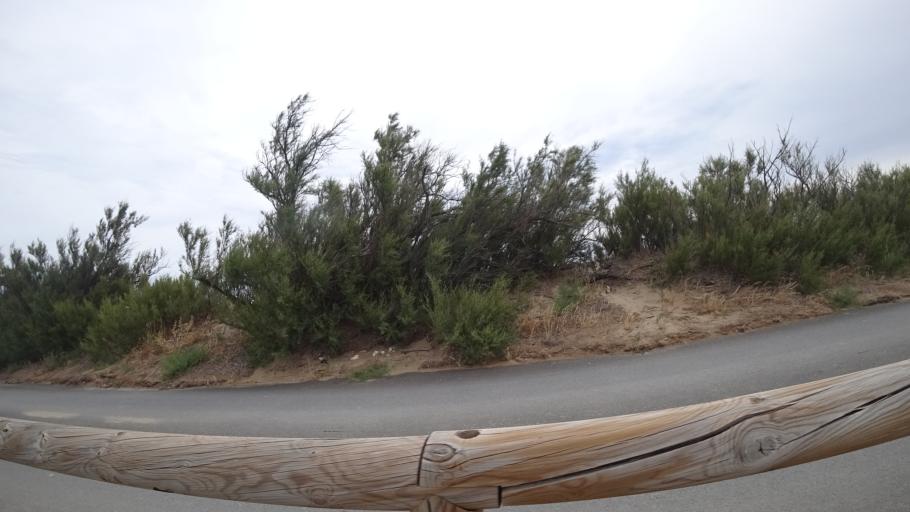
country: FR
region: Languedoc-Roussillon
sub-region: Departement de l'Aude
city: Leucate
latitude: 42.8905
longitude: 3.0495
